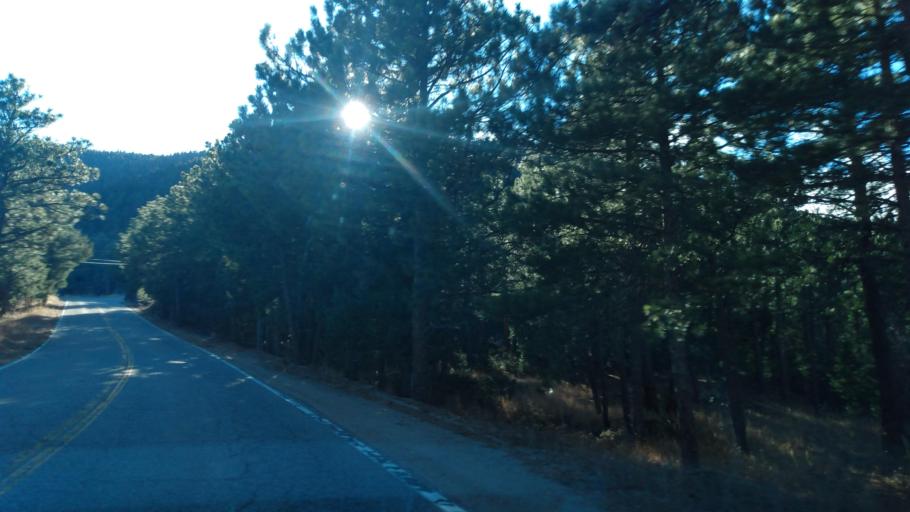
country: US
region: Colorado
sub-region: Boulder County
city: Coal Creek
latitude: 39.9883
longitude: -105.3729
